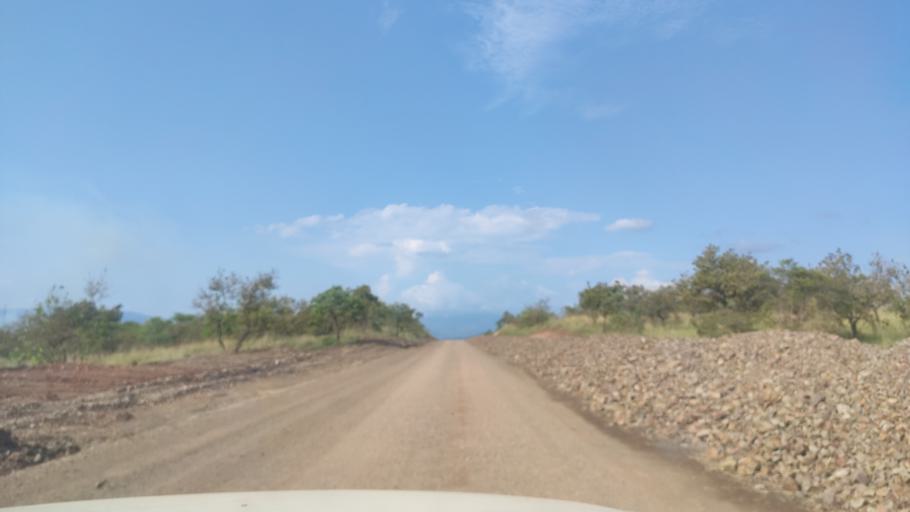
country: ET
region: Southern Nations, Nationalities, and People's Region
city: Felege Neway
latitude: 6.4289
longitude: 37.2634
